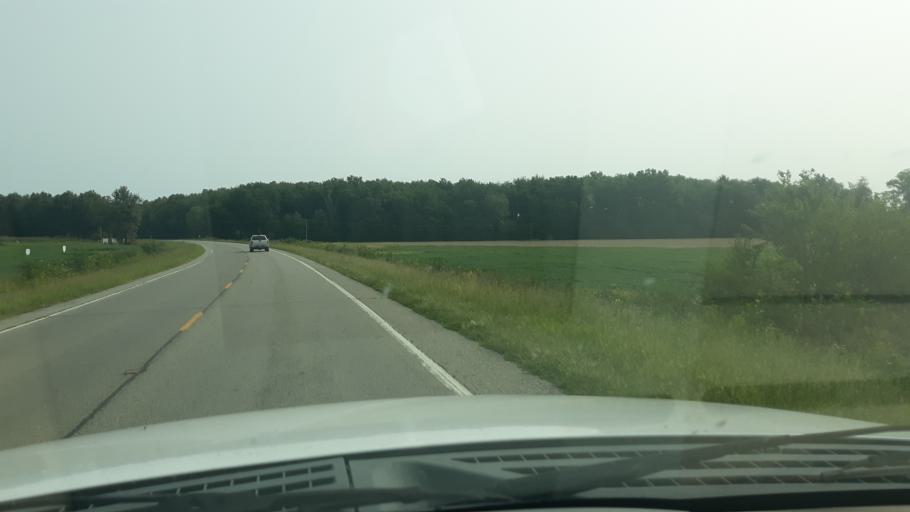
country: US
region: Illinois
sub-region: White County
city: Norris City
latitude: 37.9685
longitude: -88.3238
